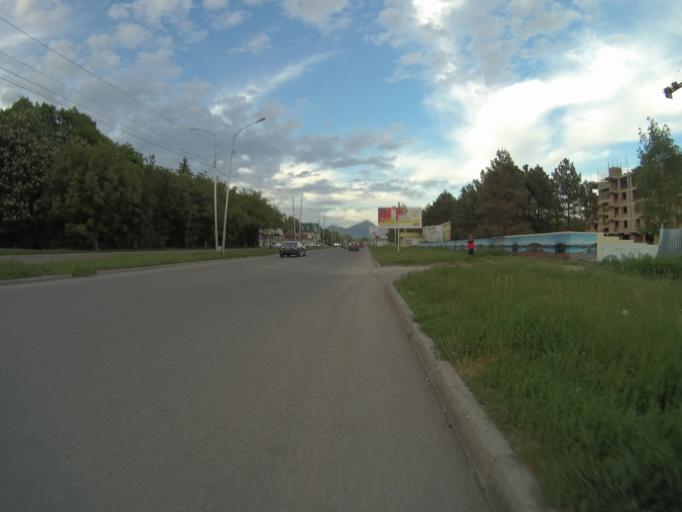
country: RU
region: Stavropol'skiy
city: Yessentukskaya
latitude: 44.0509
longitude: 42.8984
